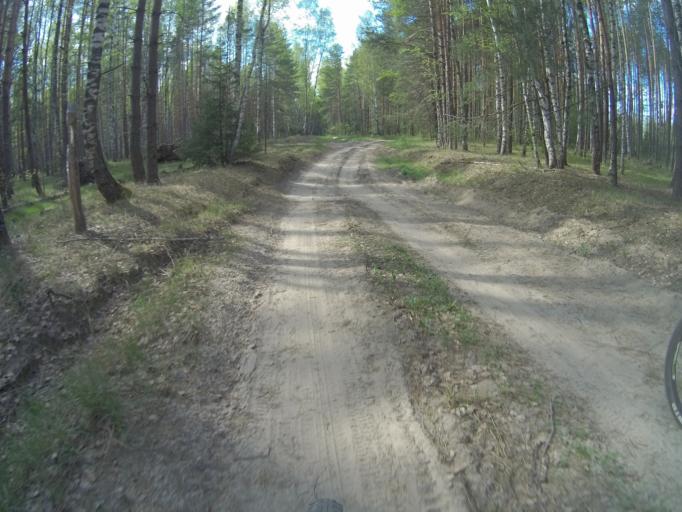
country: RU
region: Vladimir
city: Vorsha
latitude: 55.9639
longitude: 40.1877
